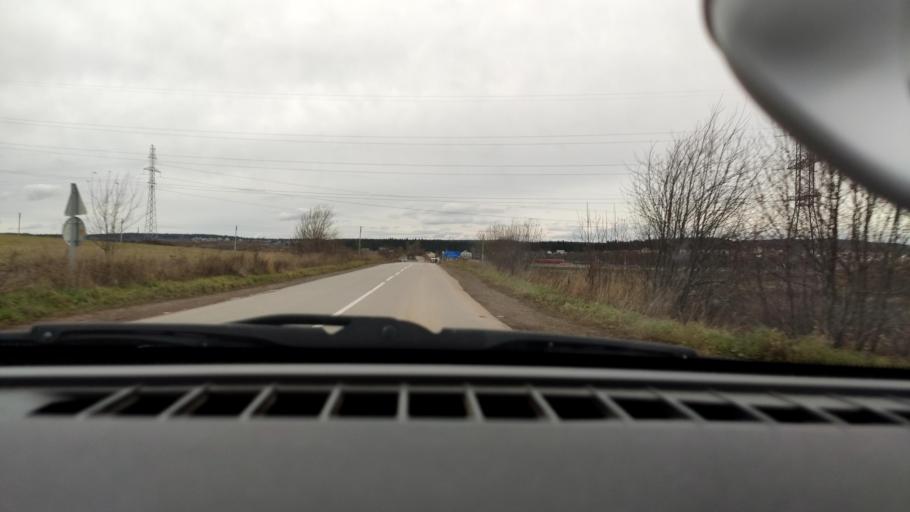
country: RU
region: Perm
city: Ferma
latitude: 57.9277
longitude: 56.3320
